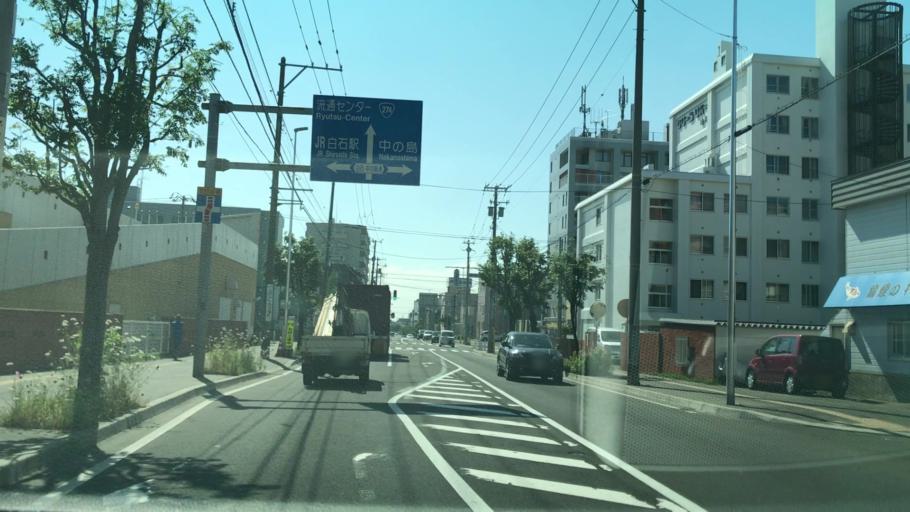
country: JP
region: Hokkaido
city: Sapporo
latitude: 43.0523
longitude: 141.4112
